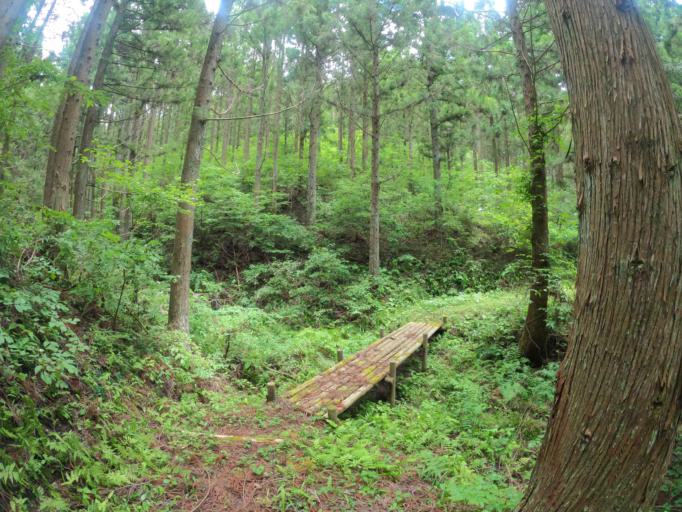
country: JP
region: Miyagi
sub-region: Oshika Gun
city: Onagawa Cho
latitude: 38.6855
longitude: 141.3524
